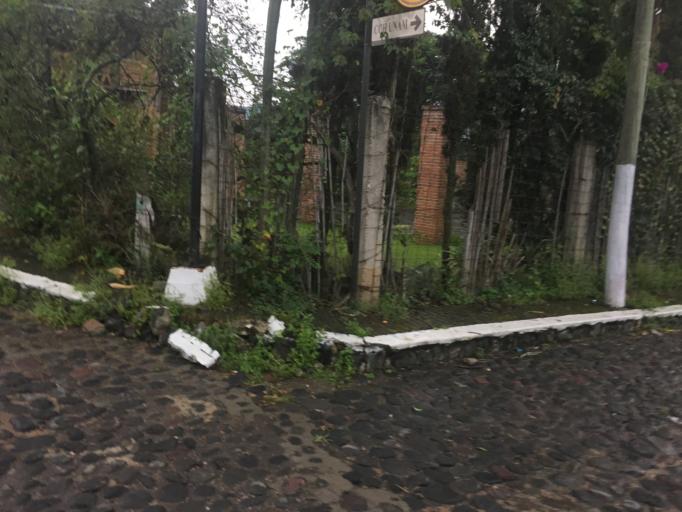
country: MX
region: Morelos
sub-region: Tlayacapan
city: Tlayacapan
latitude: 18.9539
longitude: -98.9758
